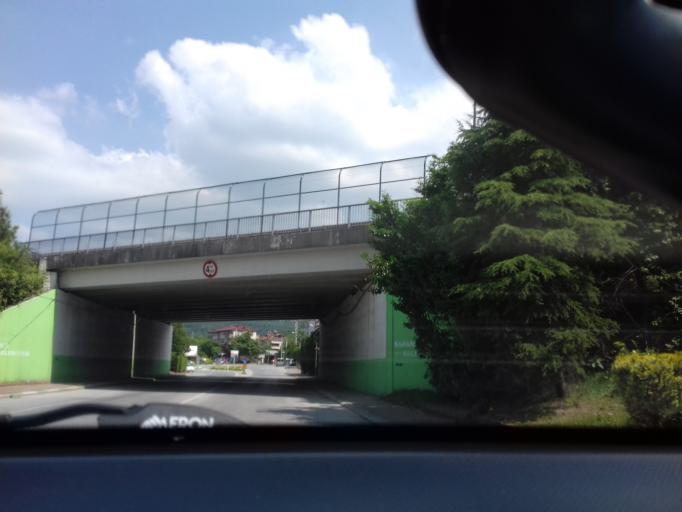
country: TR
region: Sakarya
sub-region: Merkez
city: Sapanca
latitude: 40.6889
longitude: 30.2782
